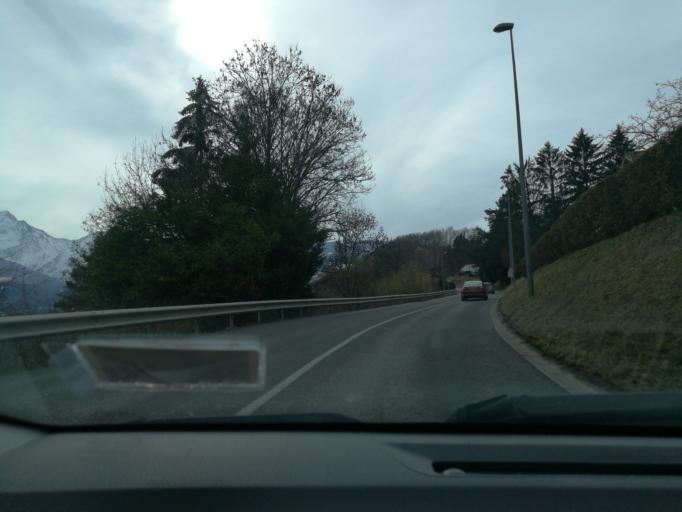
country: FR
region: Rhone-Alpes
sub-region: Departement de la Haute-Savoie
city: Sallanches
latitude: 45.9311
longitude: 6.6312
